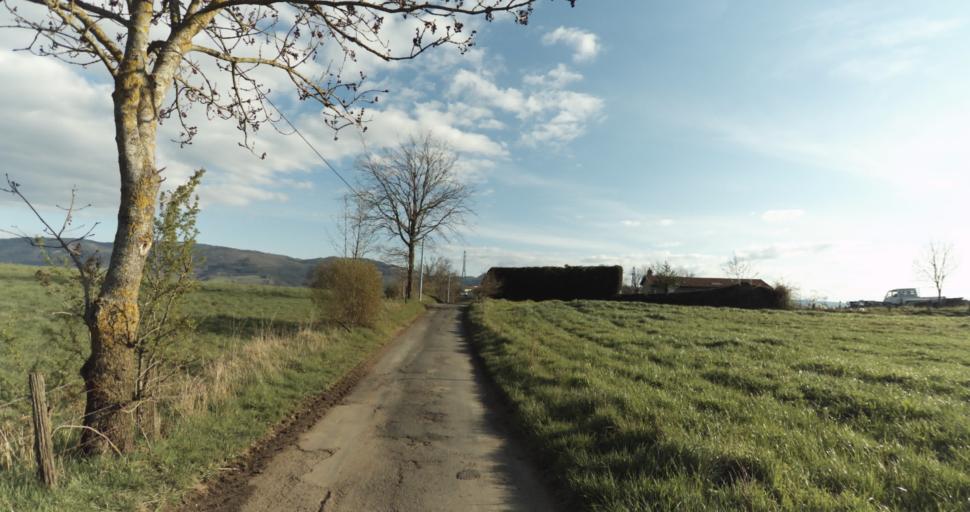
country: FR
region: Rhone-Alpes
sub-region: Departement de la Loire
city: Saint-Jean-Bonnefonds
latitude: 45.4616
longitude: 4.4411
